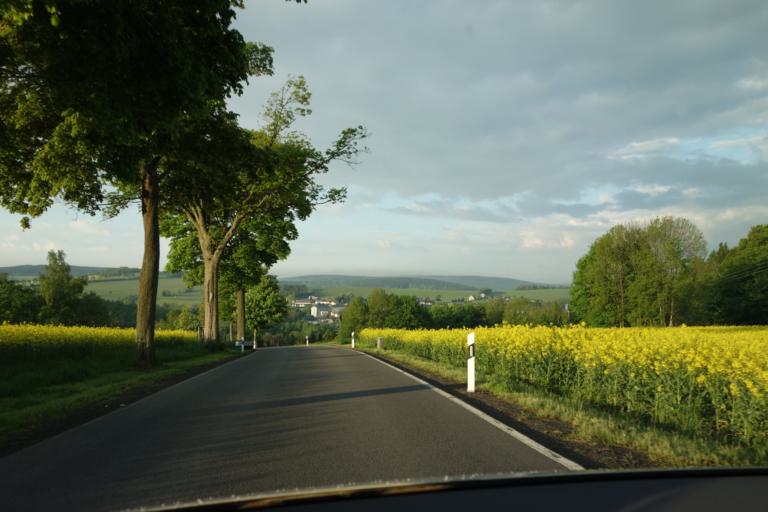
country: DE
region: Saxony
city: Zoblitz
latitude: 50.6651
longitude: 13.2392
